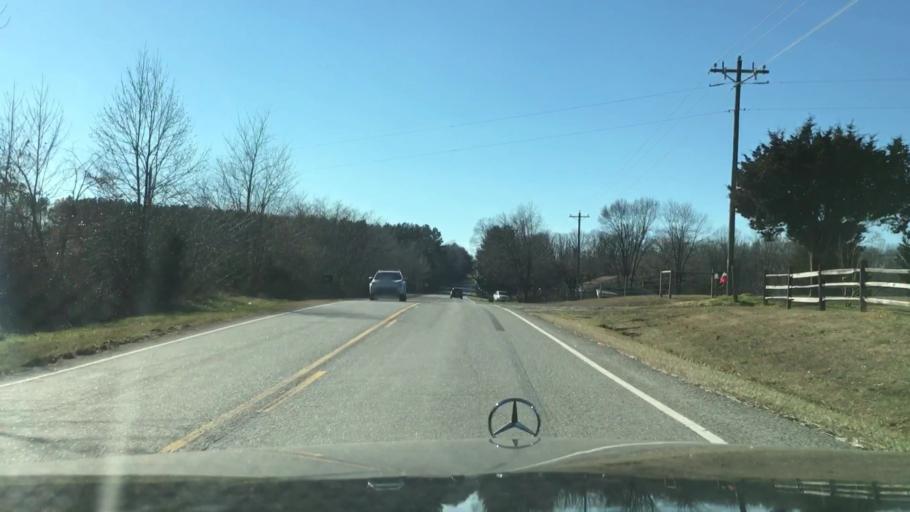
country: US
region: Virginia
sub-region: City of Bedford
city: Bedford
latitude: 37.2238
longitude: -79.5019
